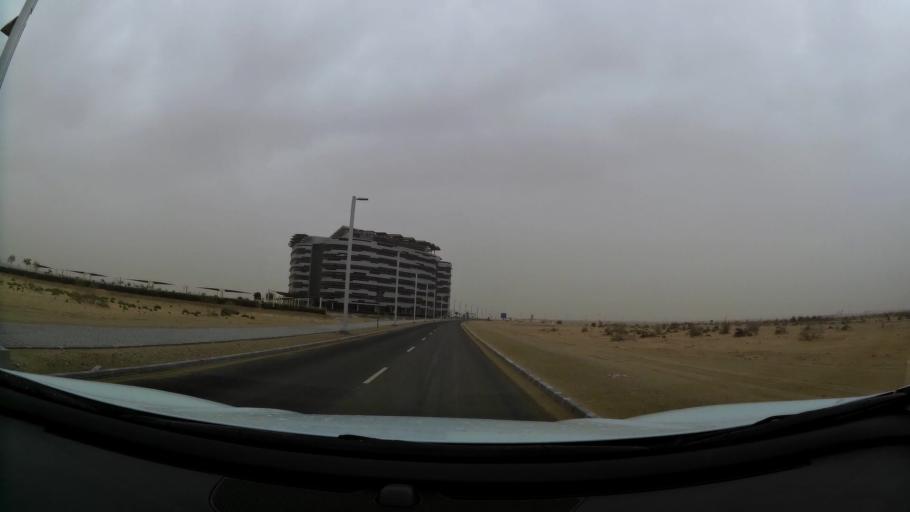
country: AE
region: Abu Dhabi
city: Abu Dhabi
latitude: 24.4288
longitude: 54.6173
